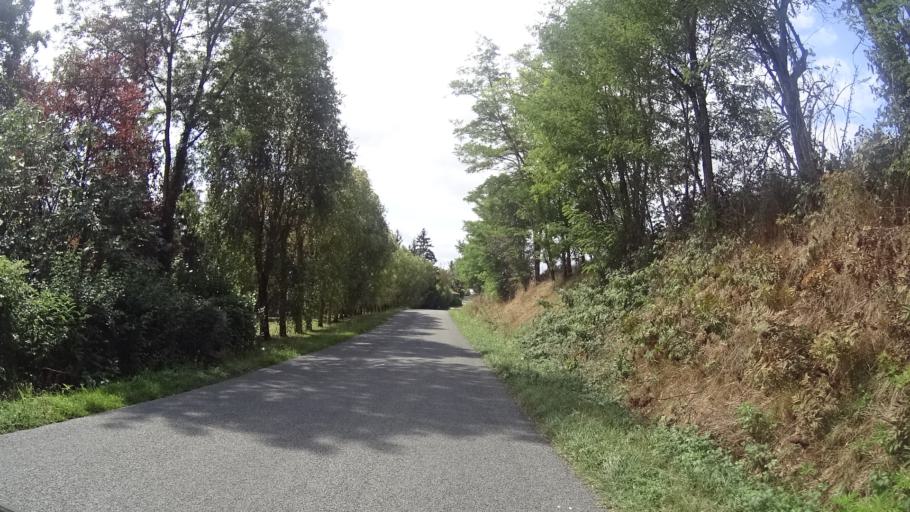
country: FR
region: Aquitaine
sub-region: Departement du Lot-et-Garonne
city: Pont-du-Casse
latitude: 44.2553
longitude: 0.6947
